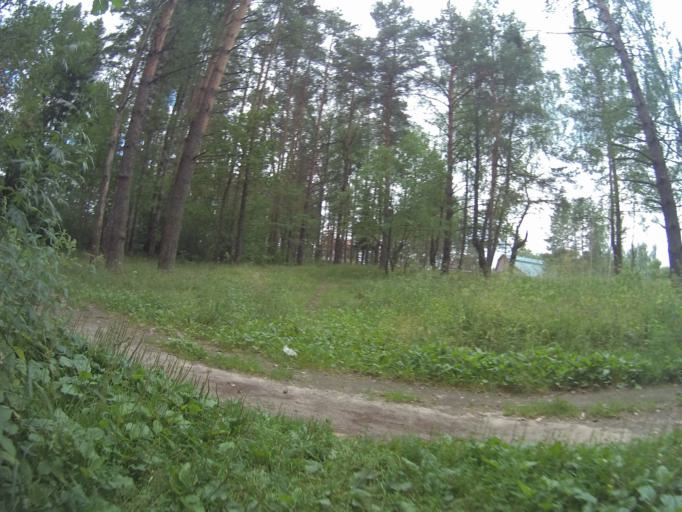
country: RU
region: Vladimir
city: Kommunar
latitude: 56.0624
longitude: 40.4946
